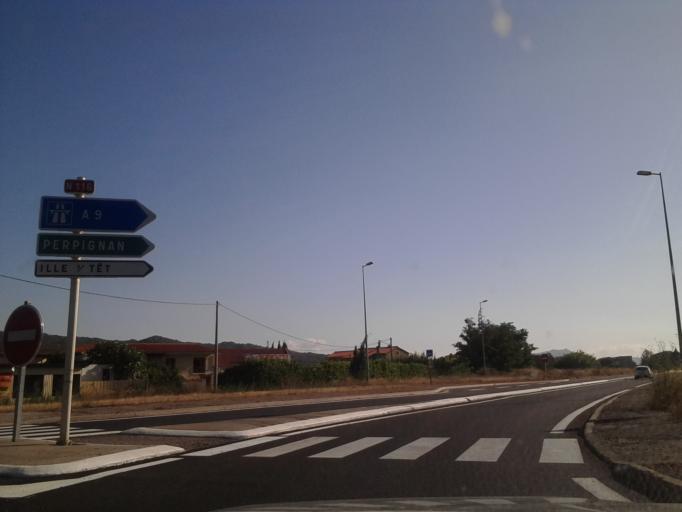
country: FR
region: Languedoc-Roussillon
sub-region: Departement des Pyrenees-Orientales
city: Ille-sur-Tet
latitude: 42.6564
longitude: 2.5861
